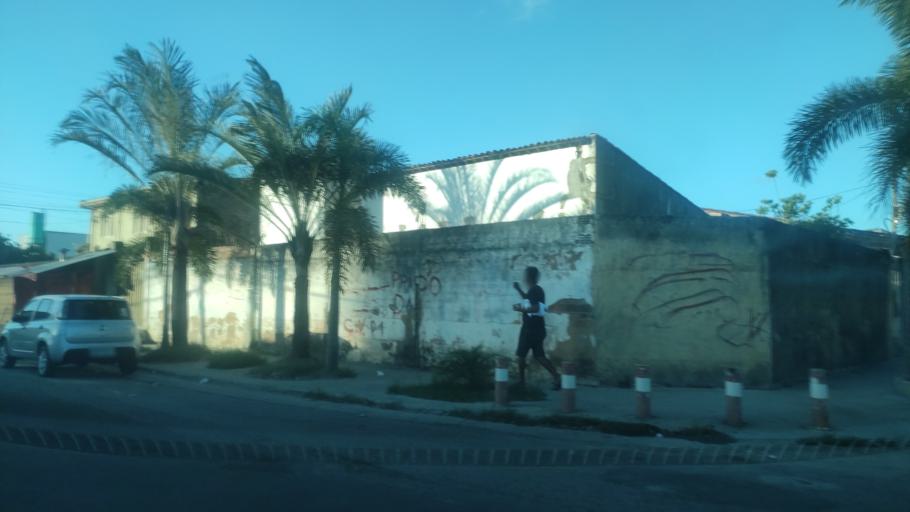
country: BR
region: Alagoas
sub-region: Maceio
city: Maceio
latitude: -9.6739
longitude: -35.7578
